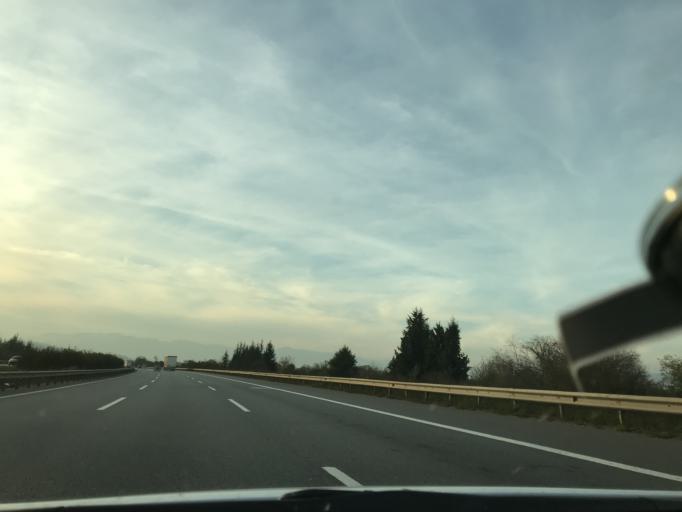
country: TR
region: Duzce
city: Cilimli
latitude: 40.8445
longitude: 31.0175
